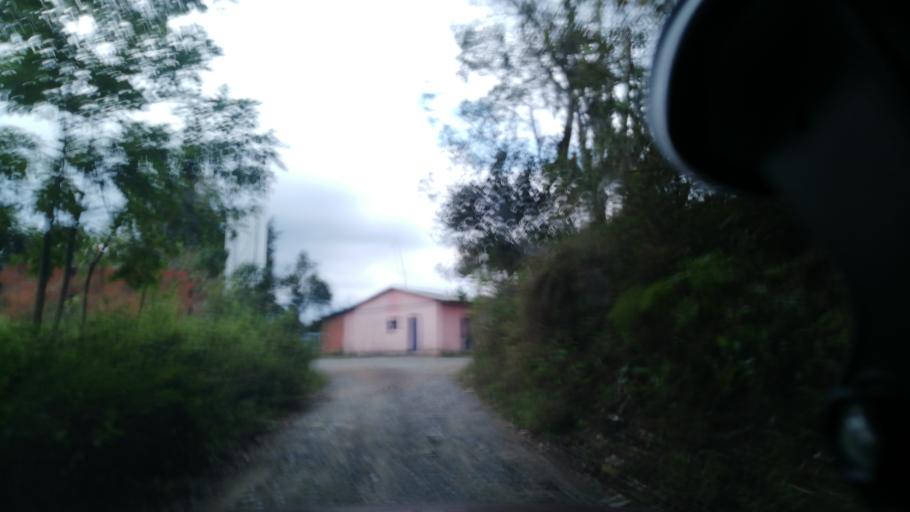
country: CO
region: Cundinamarca
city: Pacho
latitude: 5.1666
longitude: -74.2185
